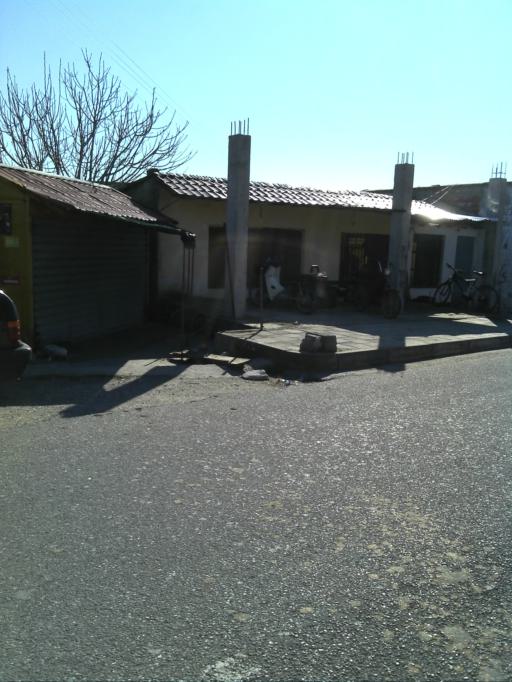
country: AL
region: Shkoder
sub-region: Rrethi i Shkodres
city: Dajc
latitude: 42.0155
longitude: 19.4412
